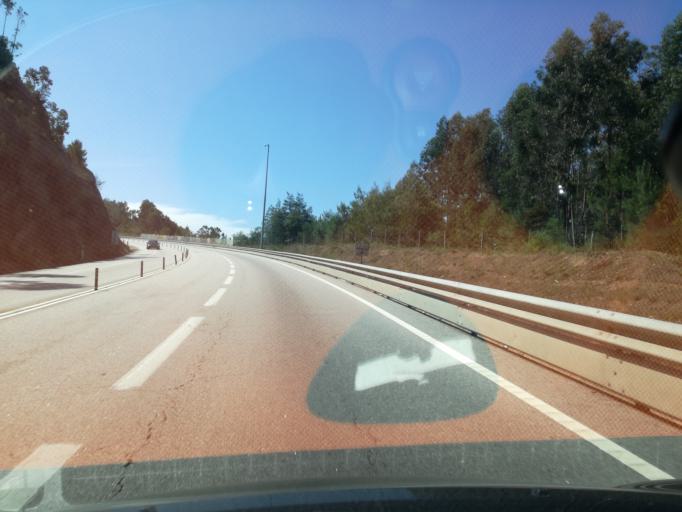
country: PT
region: Viana do Castelo
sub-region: Vila Nova de Cerveira
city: Vila Nova de Cerveira
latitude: 41.9127
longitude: -8.7829
